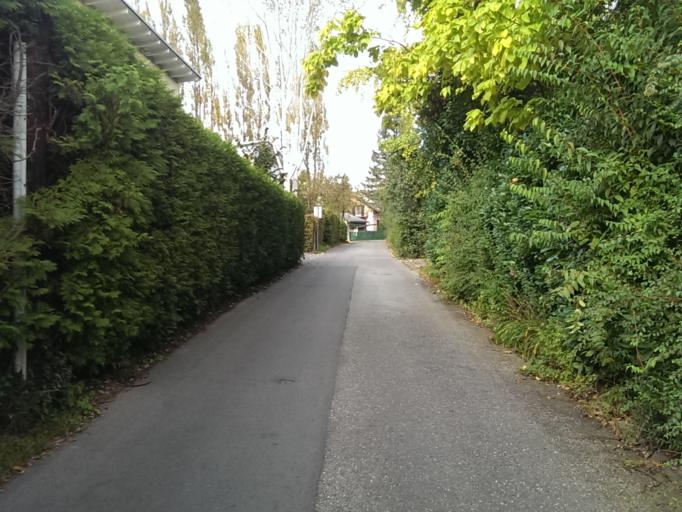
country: AT
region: Styria
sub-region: Graz Stadt
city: Graz
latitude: 47.0665
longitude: 15.4824
